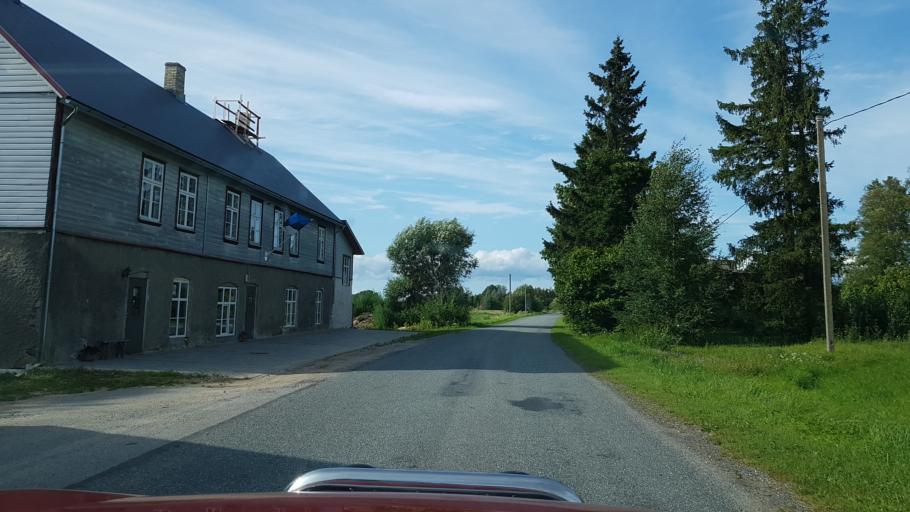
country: EE
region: Laeaene
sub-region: Lihula vald
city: Lihula
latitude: 58.4339
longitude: 24.0066
